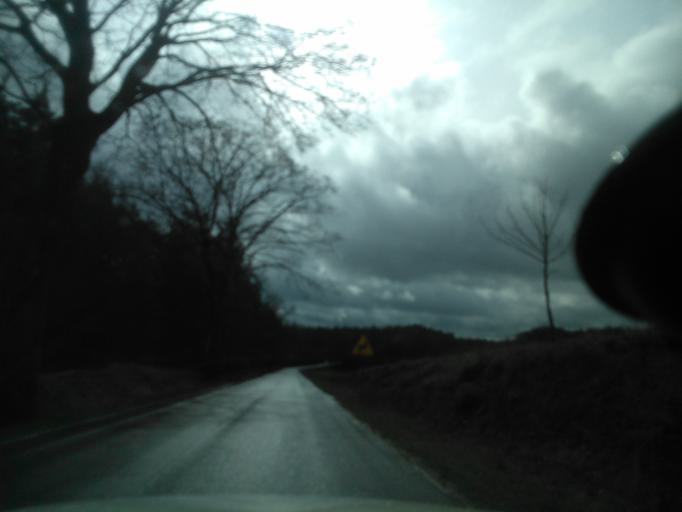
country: PL
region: Warmian-Masurian Voivodeship
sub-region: Powiat dzialdowski
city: Lidzbark
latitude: 53.2866
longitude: 19.8526
